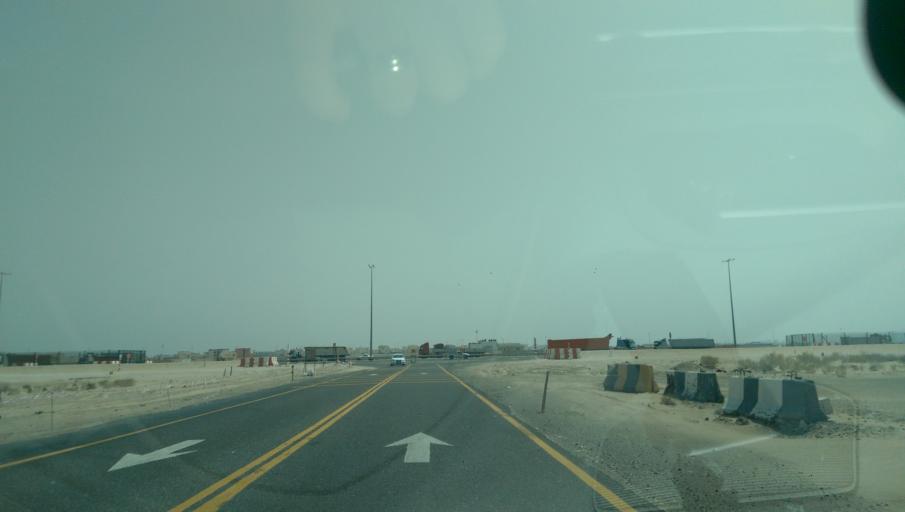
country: AE
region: Abu Dhabi
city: Abu Dhabi
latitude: 24.2987
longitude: 54.5382
